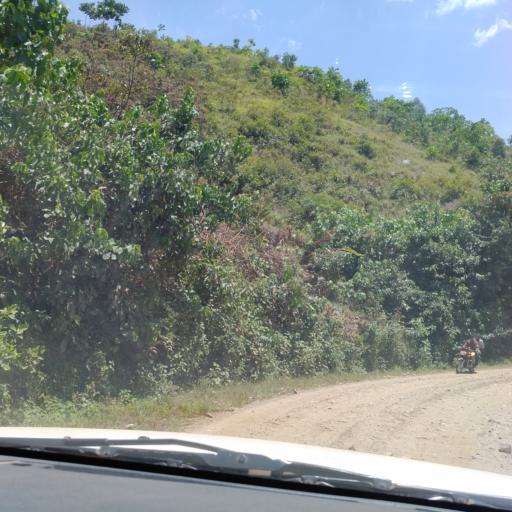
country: CD
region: Nord Kivu
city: Sake
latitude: -1.9510
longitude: 28.9272
